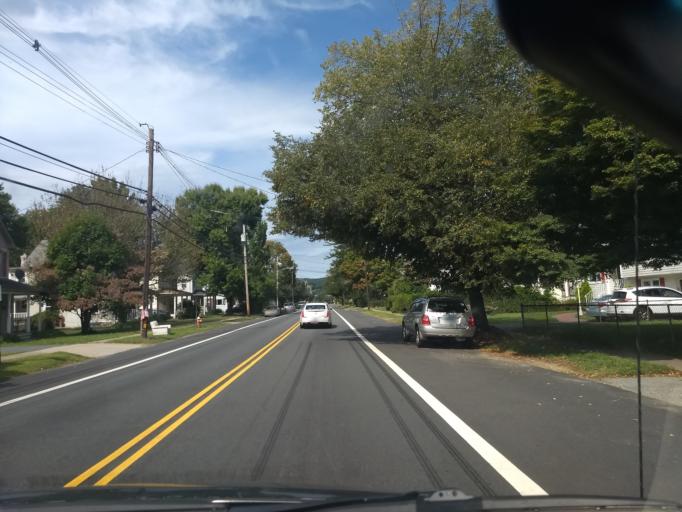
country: US
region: New Jersey
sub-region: Morris County
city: Morris Plains
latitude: 40.8228
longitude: -74.4852
